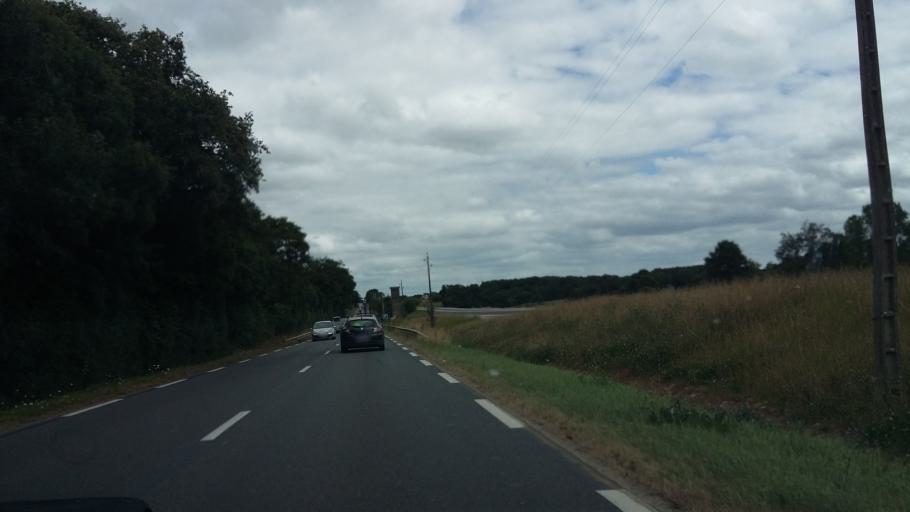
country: FR
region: Pays de la Loire
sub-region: Departement de la Vendee
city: Saint-Christophe-du-Ligneron
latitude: 46.8282
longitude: -1.7988
